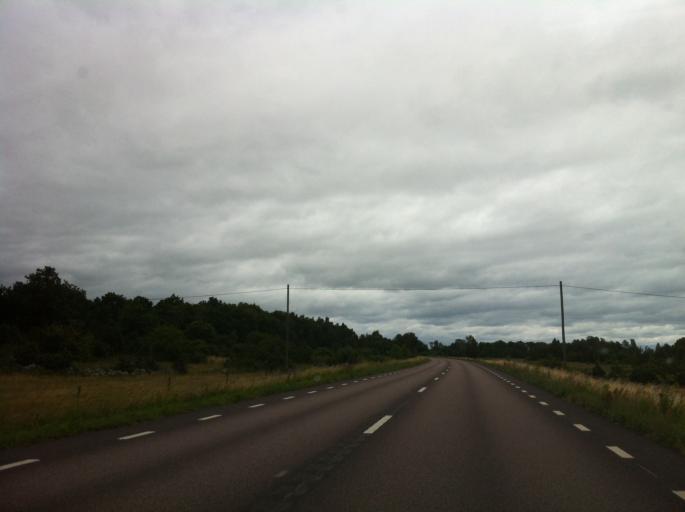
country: SE
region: Kalmar
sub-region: Borgholms Kommun
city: Borgholm
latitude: 57.0735
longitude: 16.9068
